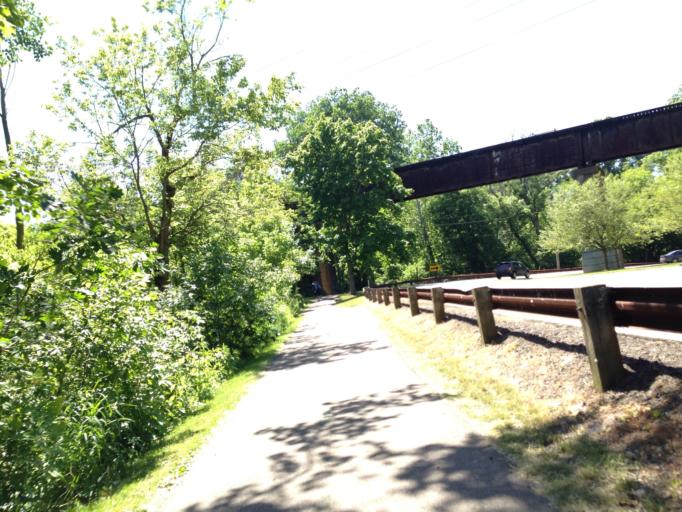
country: US
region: Ohio
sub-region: Cuyahoga County
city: Berea
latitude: 41.3466
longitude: -81.8414
